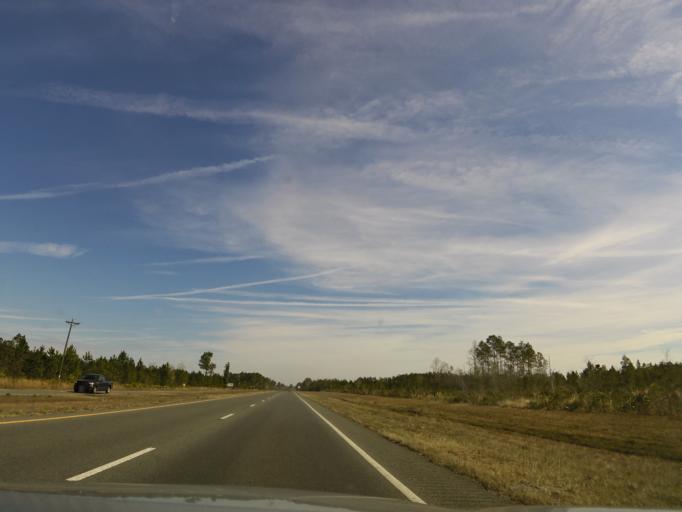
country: US
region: Georgia
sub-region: Brantley County
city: Nahunta
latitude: 31.2252
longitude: -81.8275
